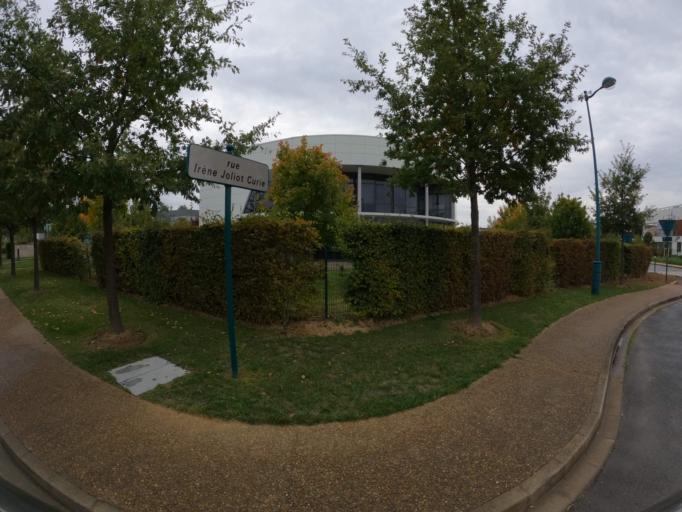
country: FR
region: Ile-de-France
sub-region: Departement de Seine-et-Marne
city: Serris
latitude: 48.8420
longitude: 2.7971
